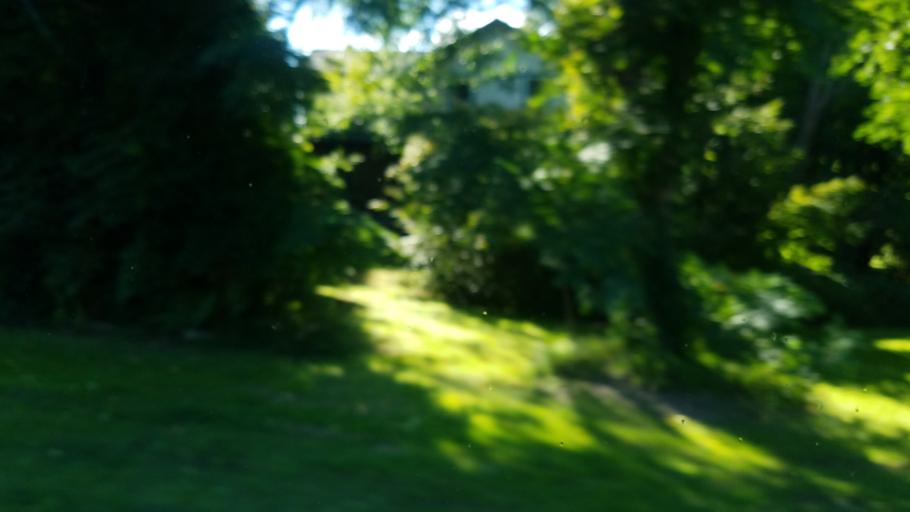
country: US
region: Ohio
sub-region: Mahoning County
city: Canfield
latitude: 41.0560
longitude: -80.7607
